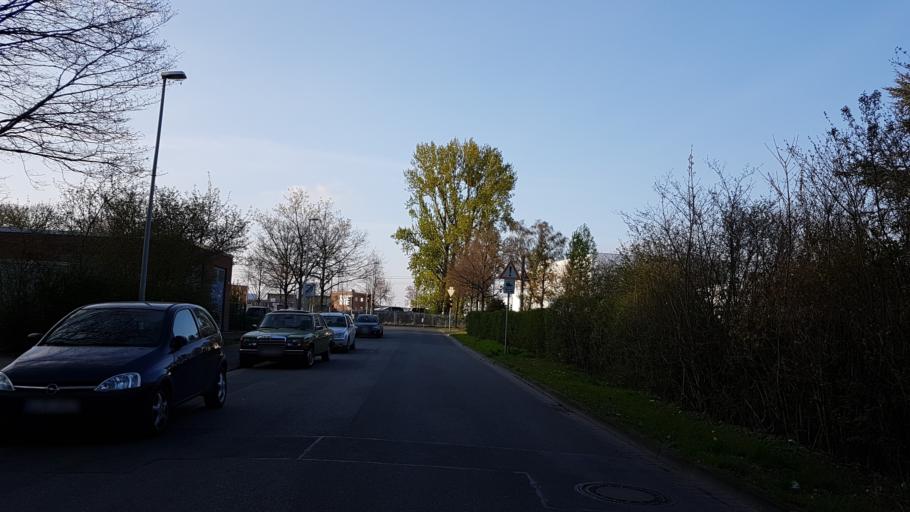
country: DE
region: Lower Saxony
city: Hannover
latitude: 52.3593
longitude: 9.6872
